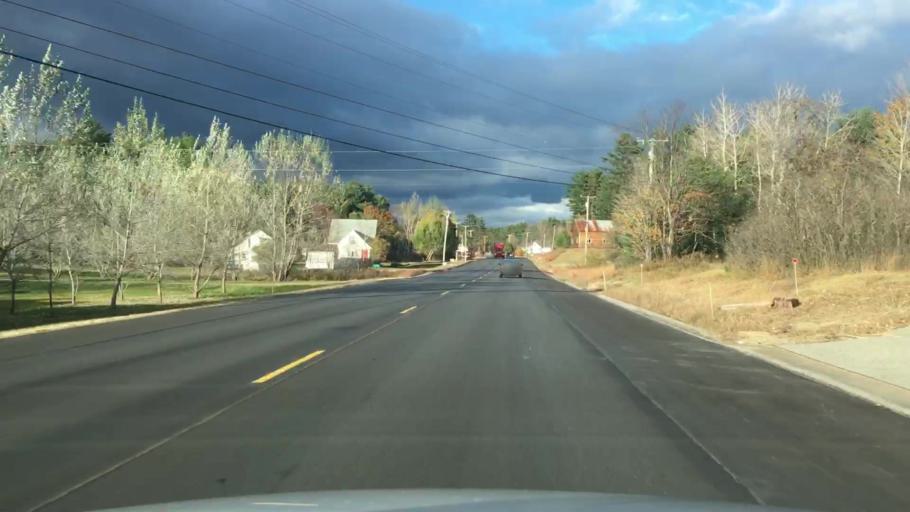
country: US
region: Maine
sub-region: Androscoggin County
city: Livermore
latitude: 44.3625
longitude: -70.2536
